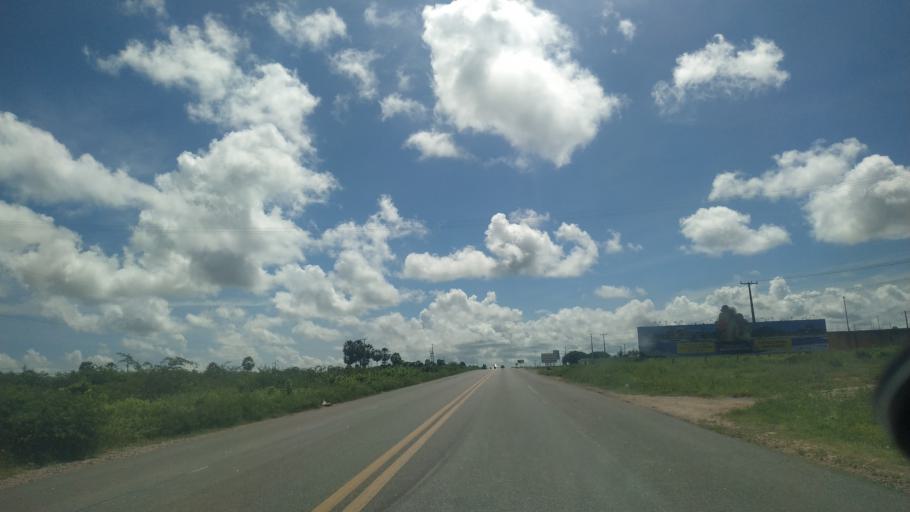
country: BR
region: Rio Grande do Norte
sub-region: Mossoro
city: Mossoro
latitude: -5.1864
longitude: -37.3028
